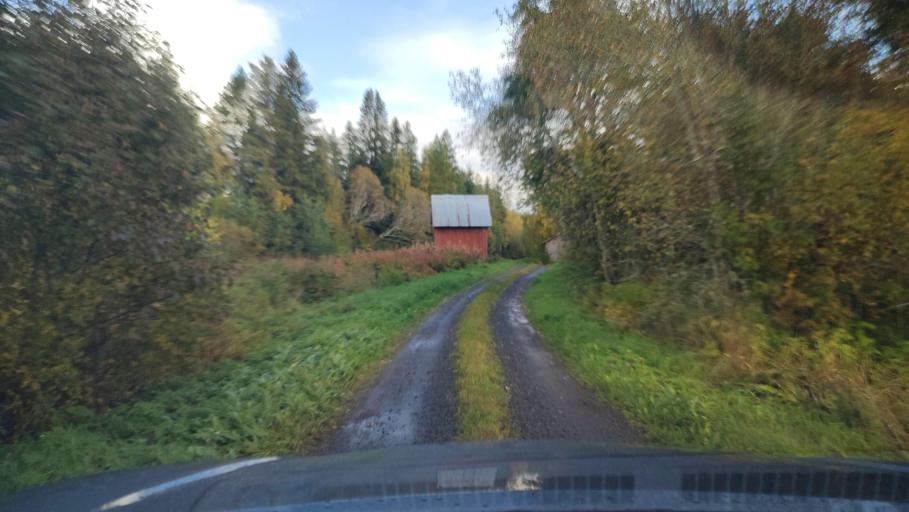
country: FI
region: Ostrobothnia
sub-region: Sydosterbotten
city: Kristinestad
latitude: 62.3063
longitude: 21.5020
